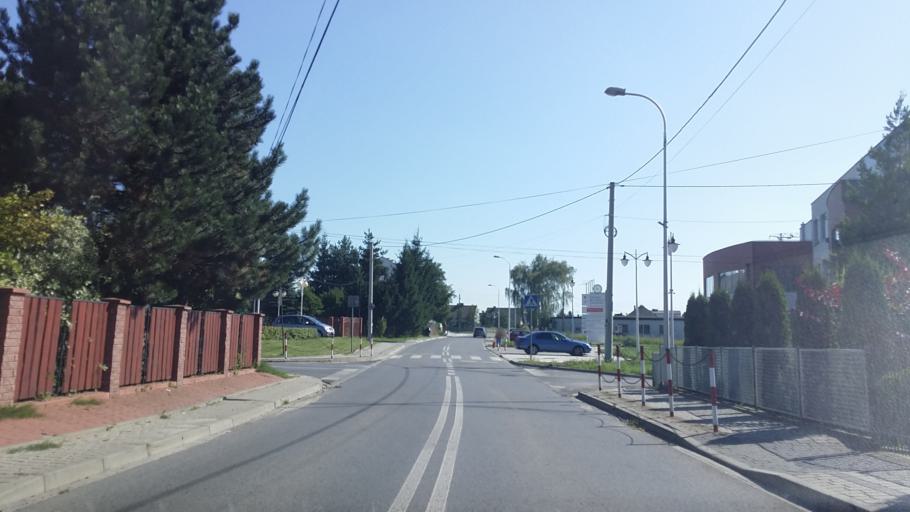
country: PL
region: Lesser Poland Voivodeship
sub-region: Powiat oswiecimski
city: Zator
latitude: 49.9949
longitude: 19.4325
